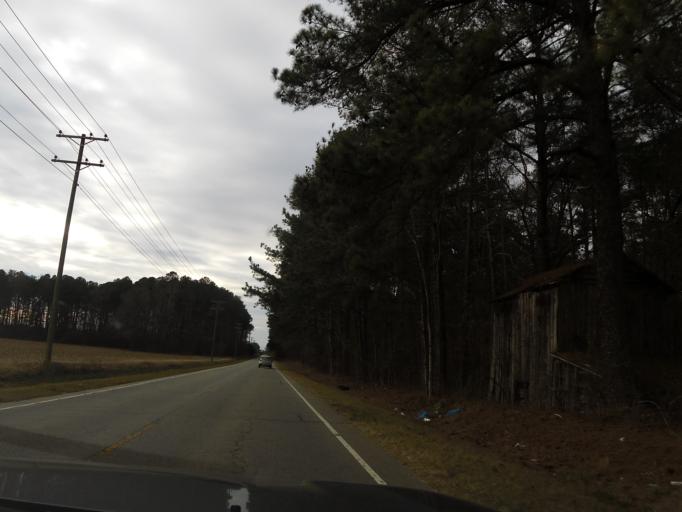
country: US
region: North Carolina
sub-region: Nash County
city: Rocky Mount
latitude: 35.9628
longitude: -77.6634
